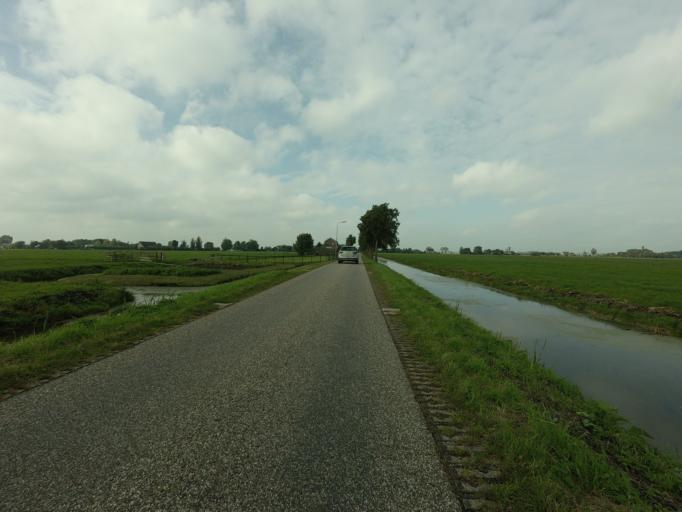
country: NL
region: South Holland
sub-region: Molenwaard
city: Liesveld
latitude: 51.8937
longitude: 4.8381
